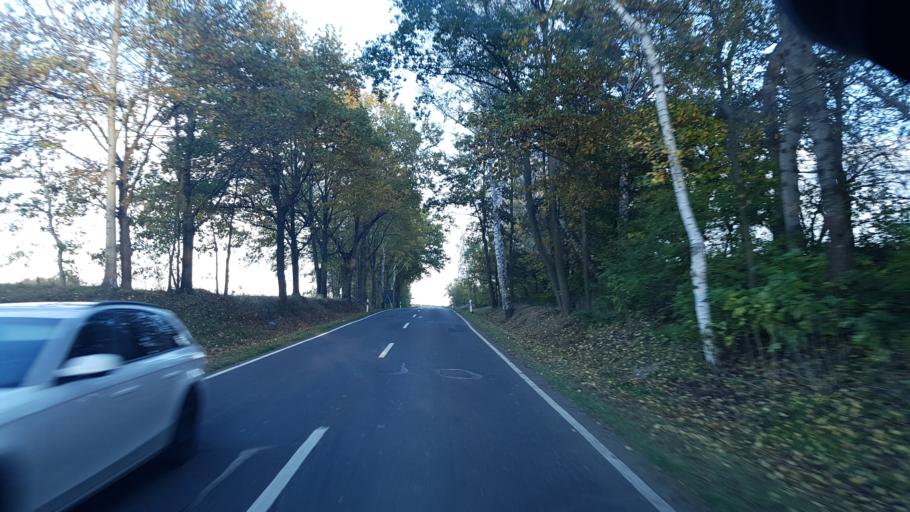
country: DE
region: Saxony
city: Belgern
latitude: 51.4407
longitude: 13.0906
